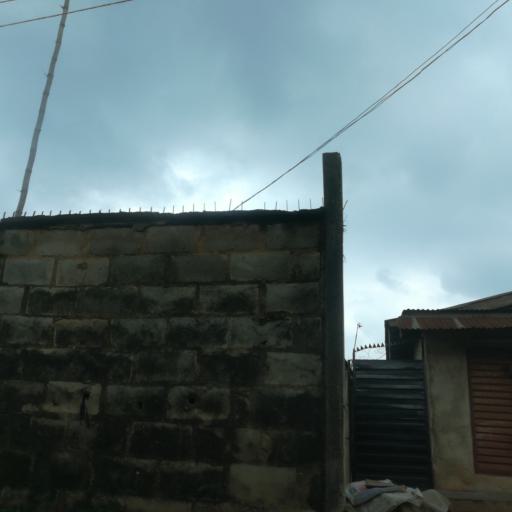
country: NG
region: Lagos
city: Agege
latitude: 6.5934
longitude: 3.3044
